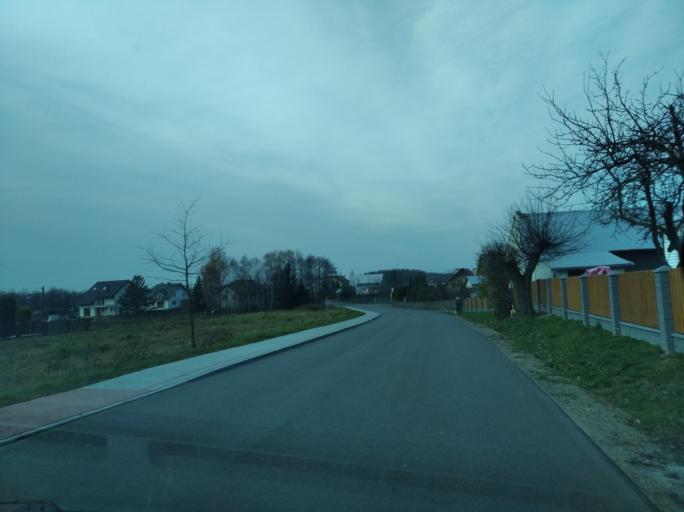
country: PL
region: Subcarpathian Voivodeship
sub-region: Powiat ropczycko-sedziszowski
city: Sedziszow Malopolski
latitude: 50.0864
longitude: 21.7094
